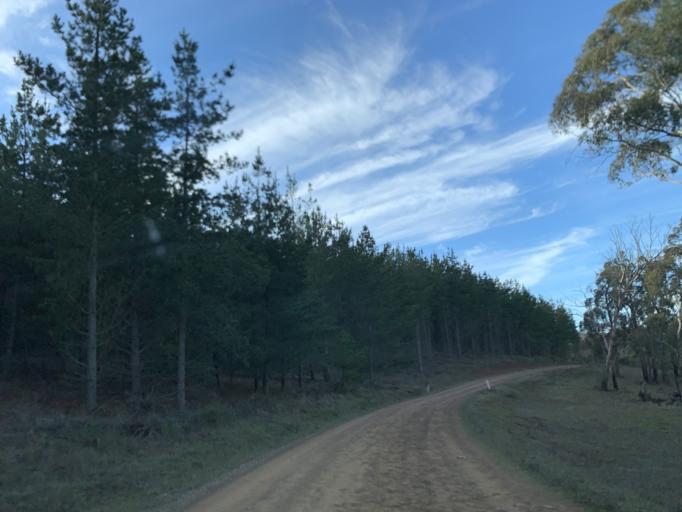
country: AU
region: Victoria
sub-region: Mansfield
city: Mansfield
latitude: -36.9202
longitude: 146.1029
